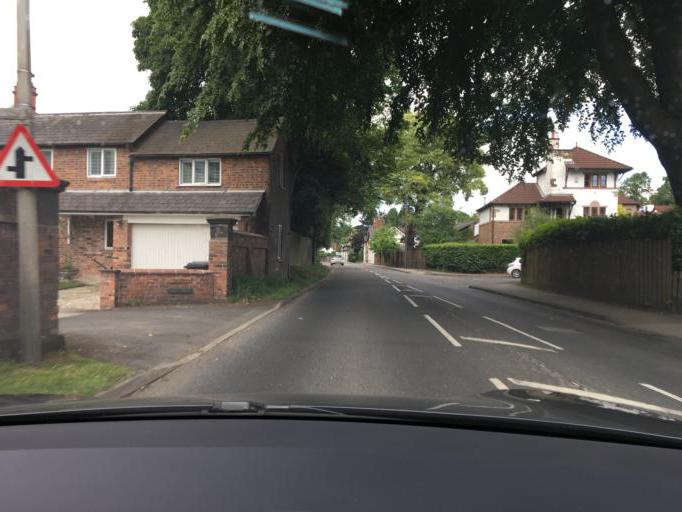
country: GB
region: England
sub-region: Cheshire East
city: Knutsford
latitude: 53.2985
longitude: -2.3624
